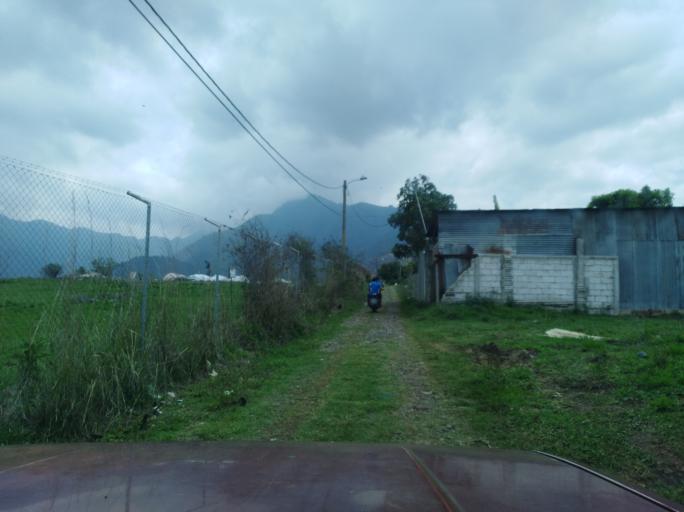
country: GT
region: Guatemala
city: Amatitlan
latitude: 14.5224
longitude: -90.6242
